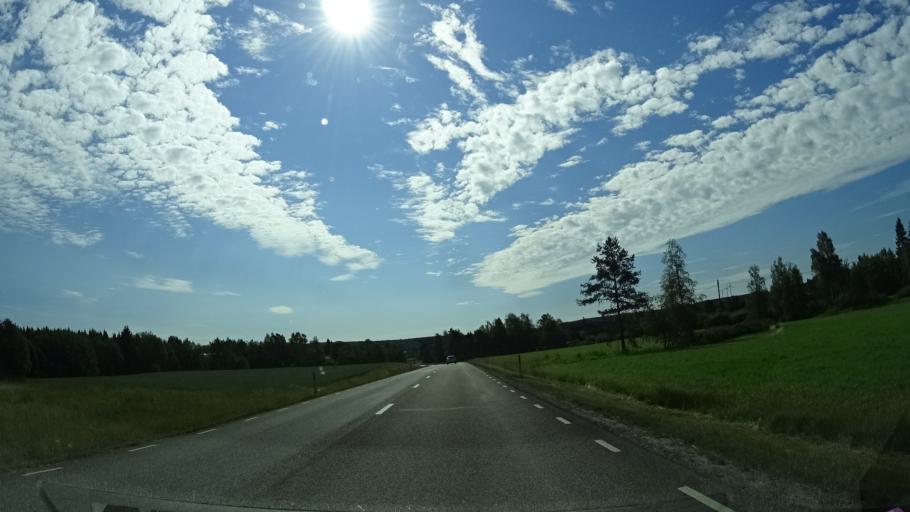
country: SE
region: Vaermland
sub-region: Arjangs Kommun
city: Toecksfors
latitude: 59.4711
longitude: 11.9876
